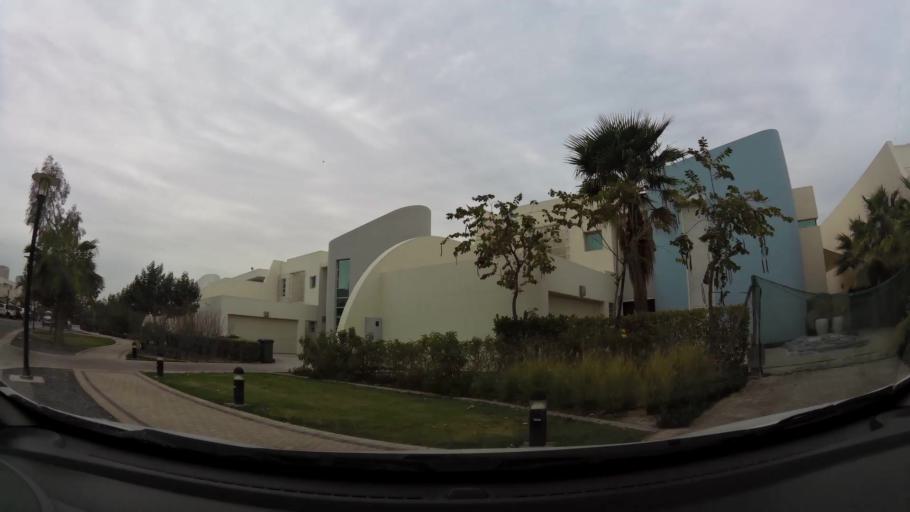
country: BH
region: Central Governorate
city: Dar Kulayb
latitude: 25.8326
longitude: 50.6205
